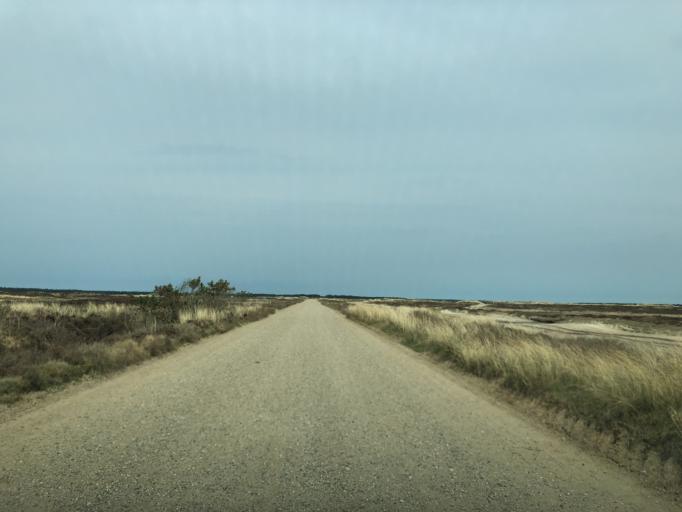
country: DK
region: South Denmark
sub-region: Varde Kommune
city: Oksbol
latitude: 55.5794
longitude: 8.1428
